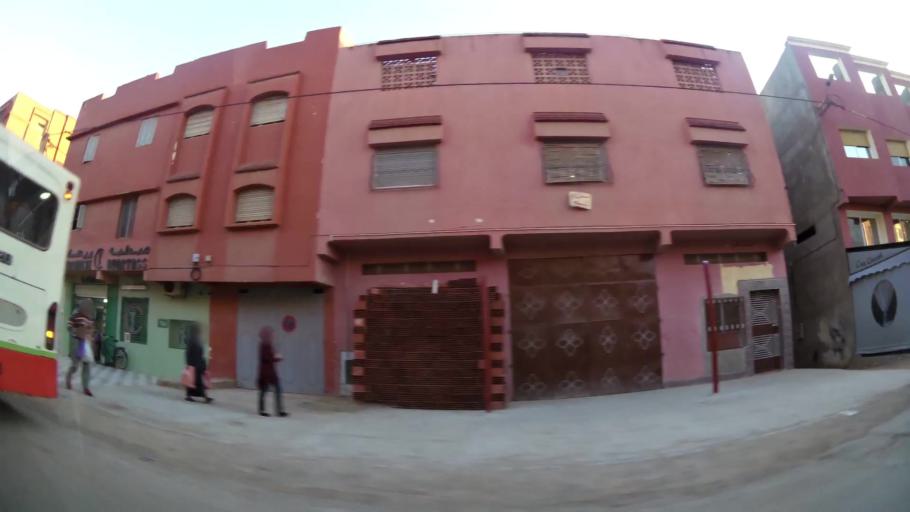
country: MA
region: Oriental
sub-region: Berkane-Taourirt
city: Berkane
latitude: 34.9131
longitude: -2.3194
